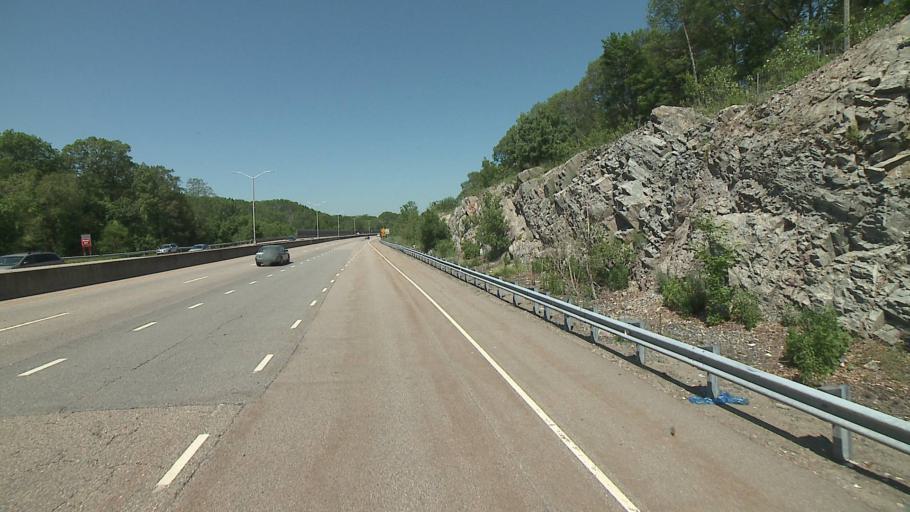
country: US
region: Connecticut
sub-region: New London County
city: Norwich
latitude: 41.4811
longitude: -72.0851
